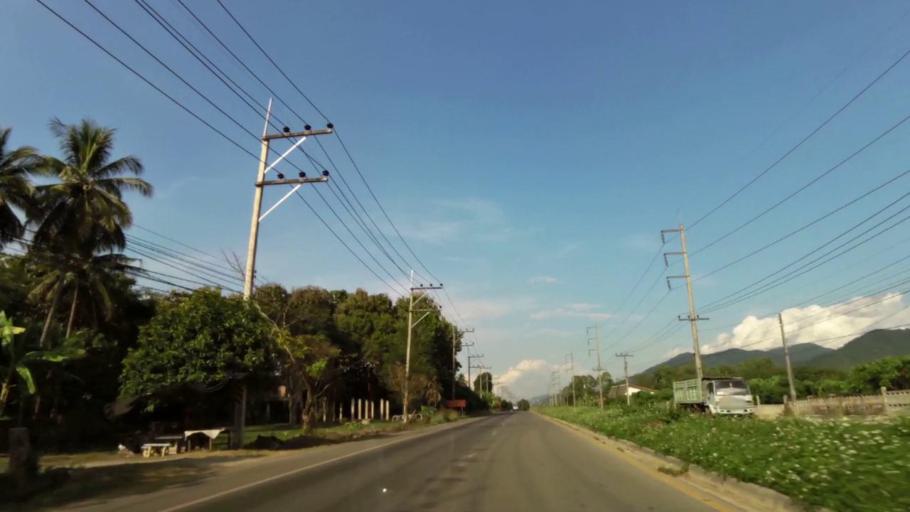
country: TH
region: Chiang Rai
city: Khun Tan
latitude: 19.8748
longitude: 100.2876
